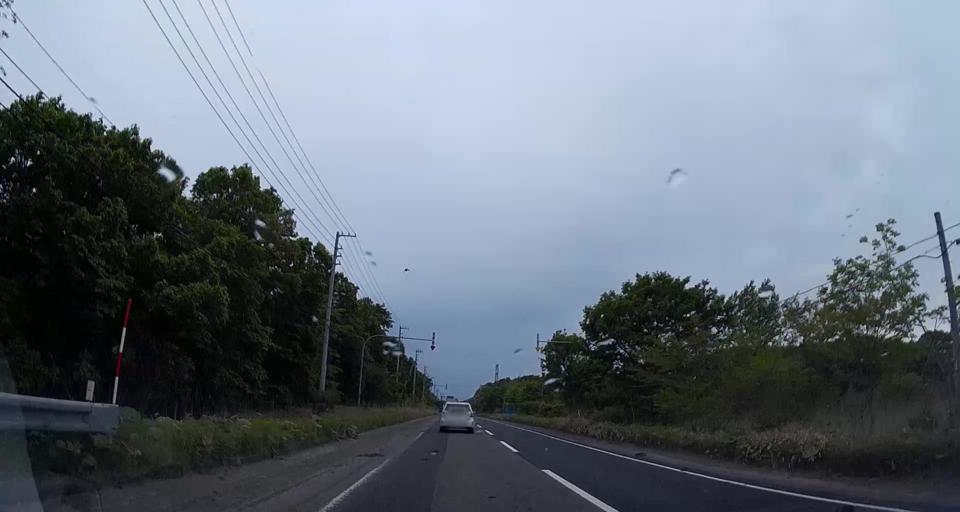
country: JP
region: Hokkaido
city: Chitose
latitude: 42.7132
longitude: 141.7513
